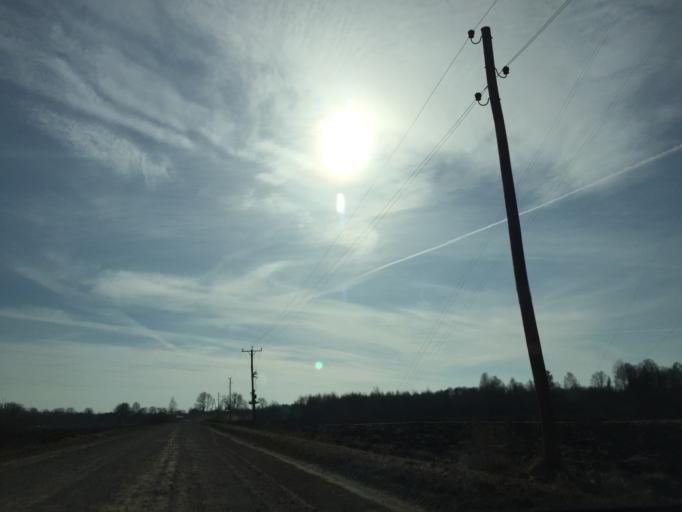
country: LV
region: Saulkrastu
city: Saulkrasti
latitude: 57.2883
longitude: 24.5111
